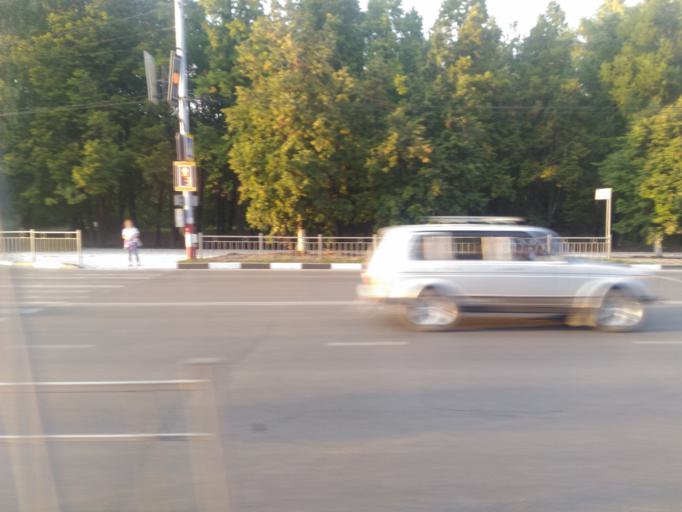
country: RU
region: Ulyanovsk
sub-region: Ulyanovskiy Rayon
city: Ulyanovsk
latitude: 54.3072
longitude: 48.3463
